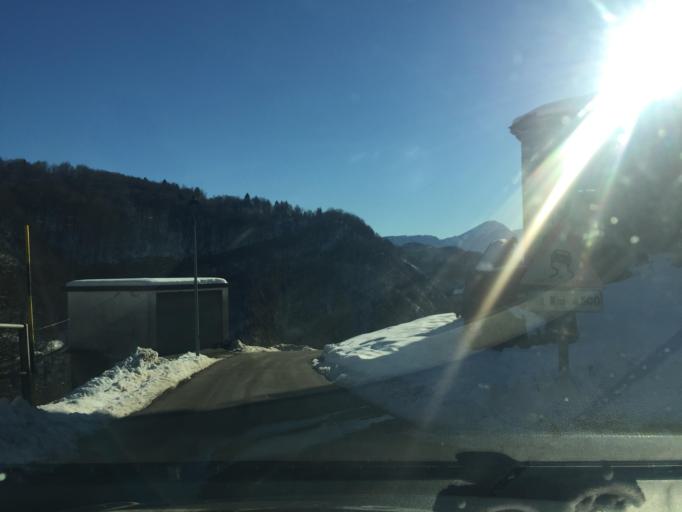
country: IT
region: Friuli Venezia Giulia
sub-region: Provincia di Udine
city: Lauco
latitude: 46.4392
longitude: 12.9684
